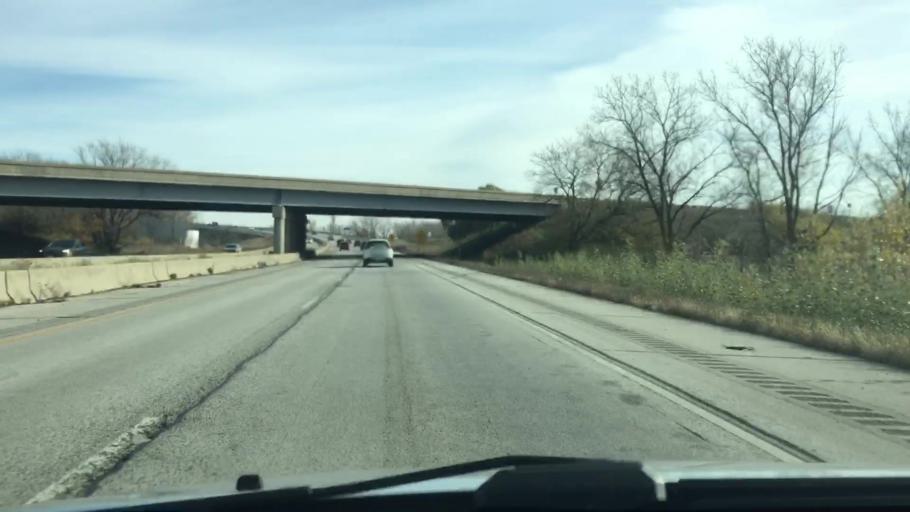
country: US
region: Wisconsin
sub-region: Brown County
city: Green Bay
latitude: 44.5400
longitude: -88.0257
